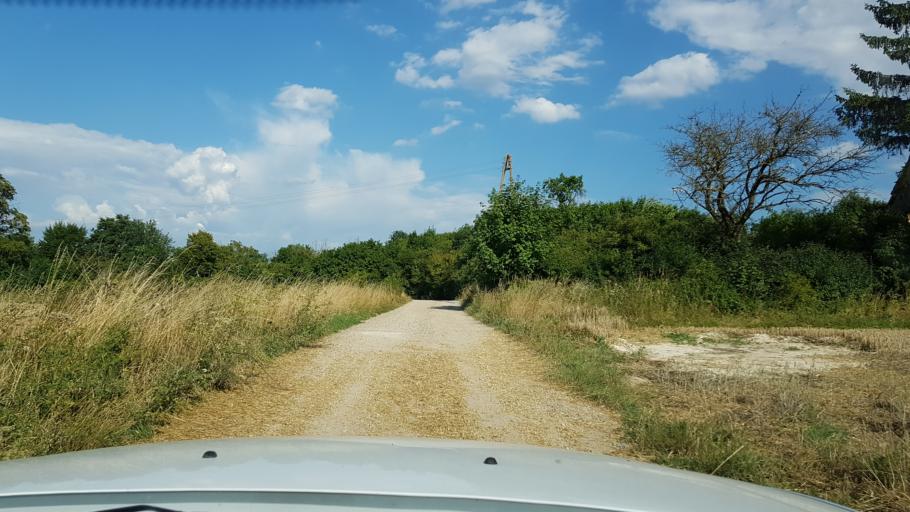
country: PL
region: West Pomeranian Voivodeship
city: Trzcinsko Zdroj
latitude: 52.9308
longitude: 14.5764
